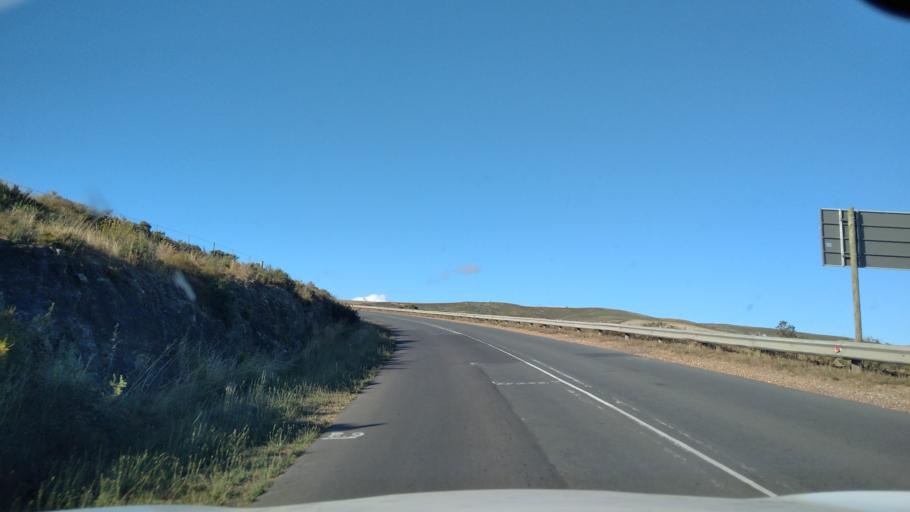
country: ZA
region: Western Cape
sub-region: Overberg District Municipality
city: Caledon
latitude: -34.1579
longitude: 19.3054
